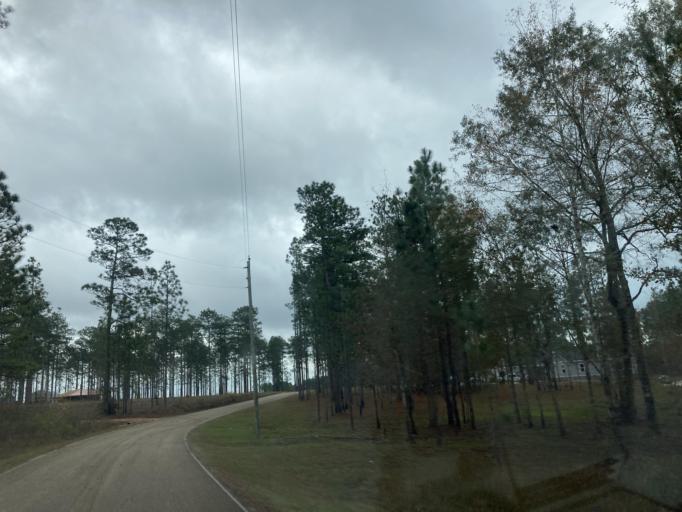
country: US
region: Mississippi
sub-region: Lamar County
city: Lumberton
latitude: 31.0961
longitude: -89.5314
